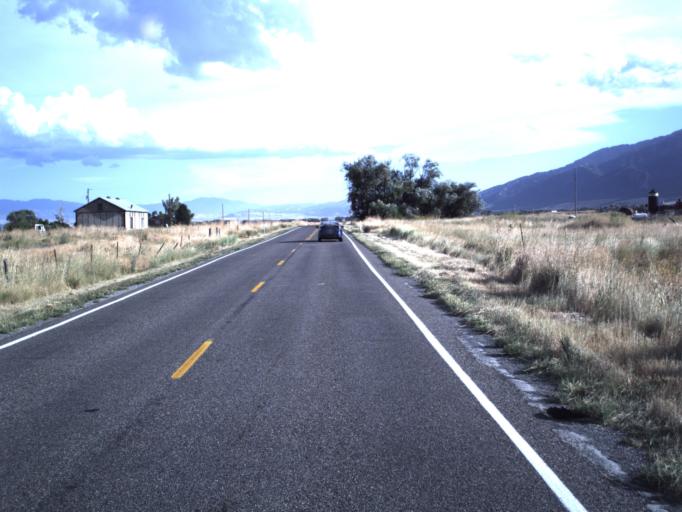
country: US
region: Utah
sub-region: Cache County
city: Benson
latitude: 41.7702
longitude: -111.9821
